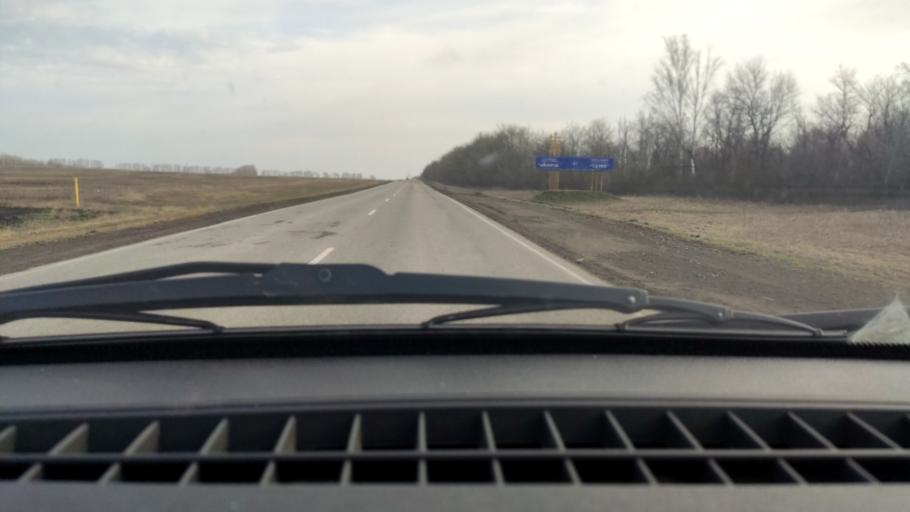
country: RU
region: Bashkortostan
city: Chishmy
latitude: 54.4675
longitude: 55.2599
